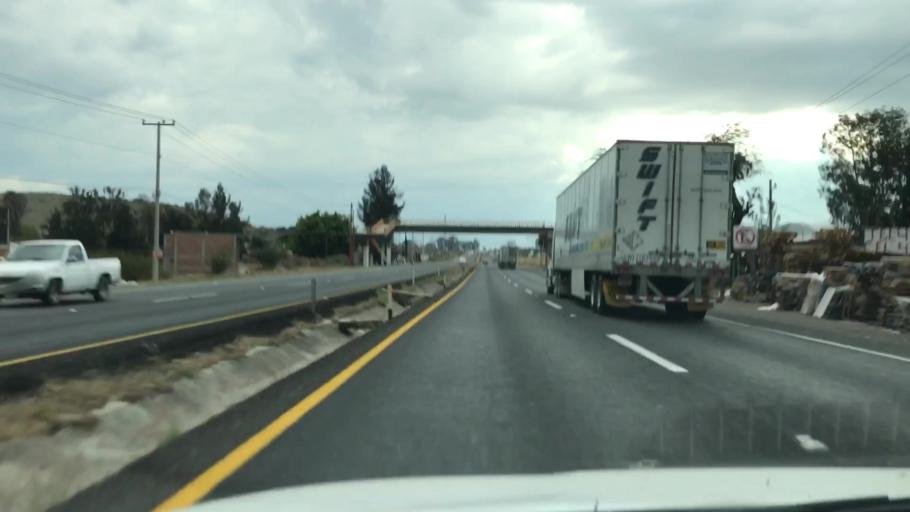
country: MX
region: Guanajuato
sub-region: Irapuato
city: Colonia Morelos de Guadalupe de Rivera
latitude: 20.5736
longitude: -101.4408
